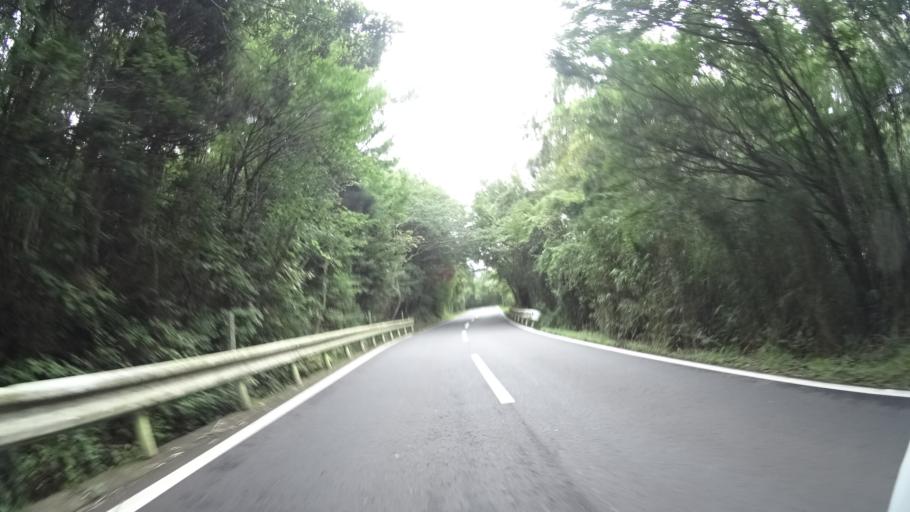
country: JP
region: Oita
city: Beppu
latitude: 33.2996
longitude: 131.3792
